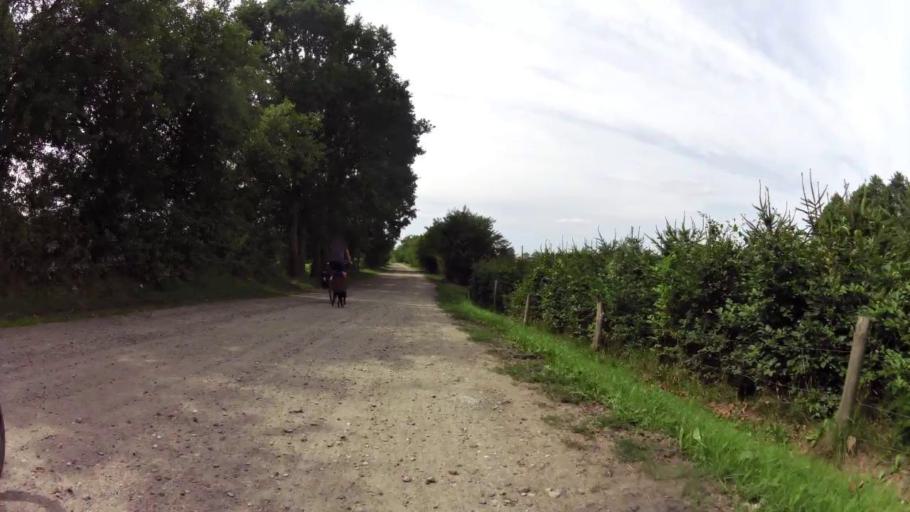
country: PL
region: West Pomeranian Voivodeship
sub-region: Powiat lobeski
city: Wegorzyno
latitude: 53.5368
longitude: 15.6090
